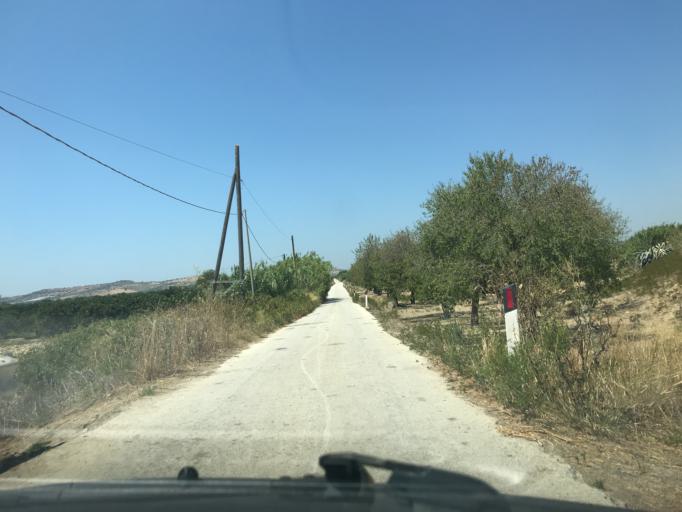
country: IT
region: Sicily
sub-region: Provincia di Siracusa
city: Noto
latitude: 36.8359
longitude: 15.0536
